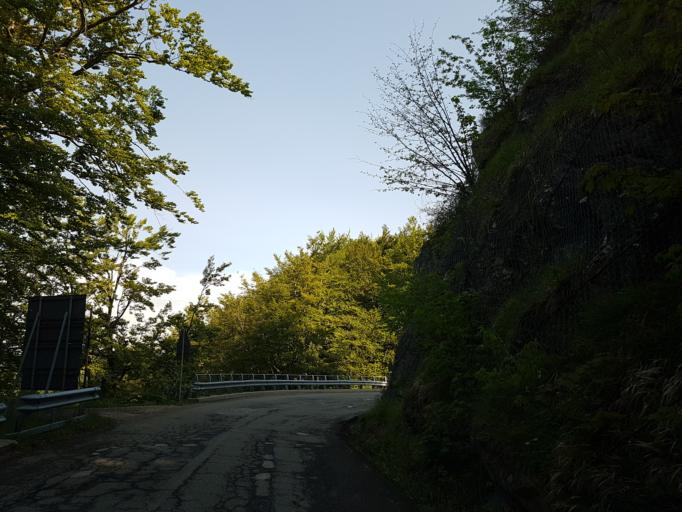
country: IT
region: Emilia-Romagna
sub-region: Forli-Cesena
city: San Piero in Bagno
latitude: 43.7980
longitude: 11.9147
